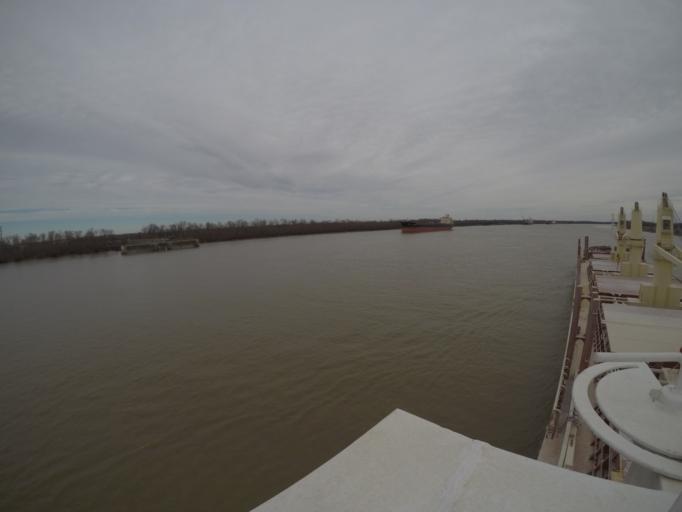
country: US
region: Louisiana
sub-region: Saint John the Baptist Parish
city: Montegut
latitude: 30.0478
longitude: -90.5186
